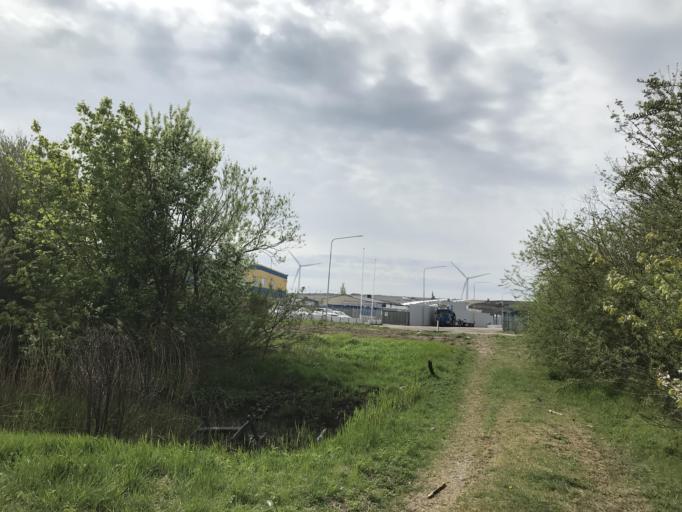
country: SE
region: Skane
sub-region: Landskrona
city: Landskrona
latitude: 55.8676
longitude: 12.8635
